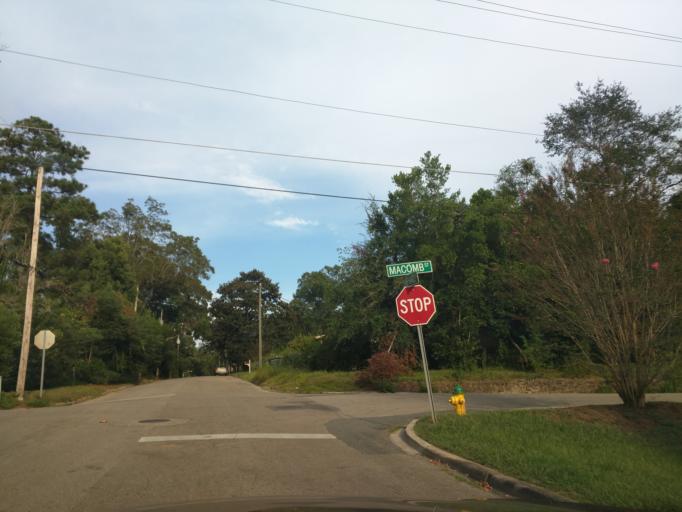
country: US
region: Florida
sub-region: Leon County
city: Tallahassee
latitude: 30.4556
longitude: -84.2880
